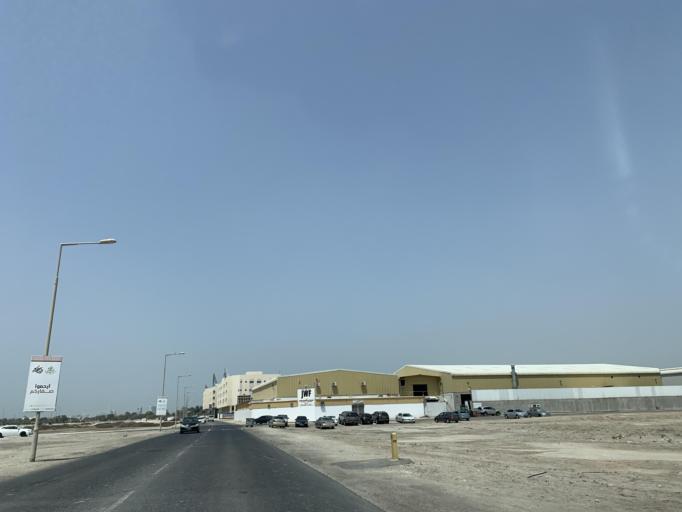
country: BH
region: Northern
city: Madinat `Isa
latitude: 26.1912
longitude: 50.5440
